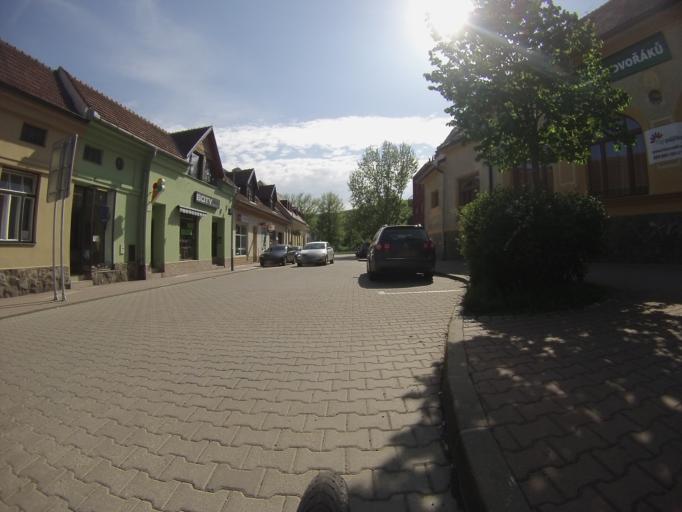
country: CZ
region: South Moravian
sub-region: Mesto Brno
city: Mokra Hora
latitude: 49.2184
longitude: 16.5542
